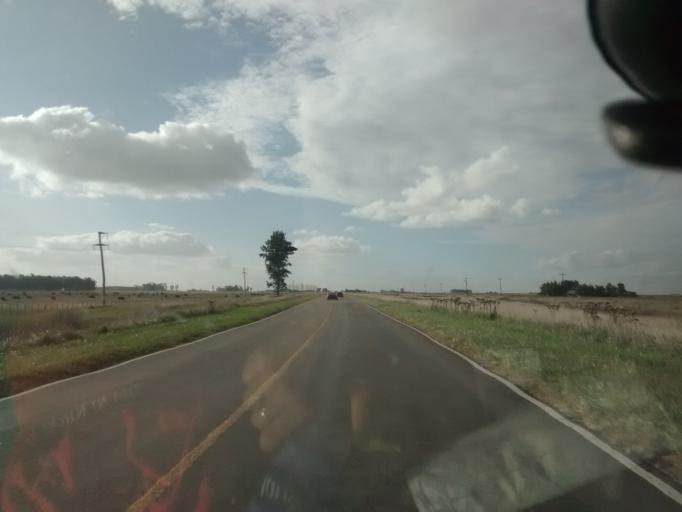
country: AR
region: Buenos Aires
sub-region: Partido de Ayacucho
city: Ayacucho
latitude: -36.9135
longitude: -58.5246
